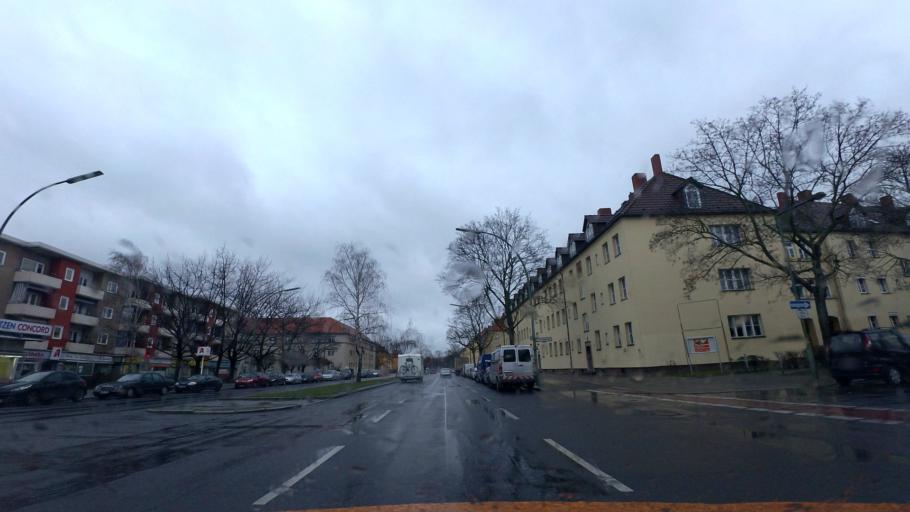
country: DE
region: Berlin
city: Spandau
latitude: 52.5471
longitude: 13.1864
